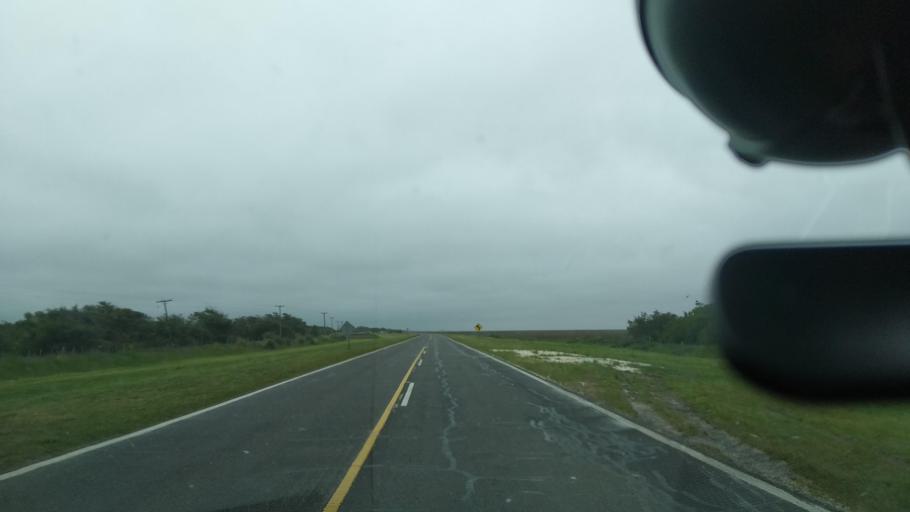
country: AR
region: Buenos Aires
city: Veronica
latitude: -35.6689
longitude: -57.3324
